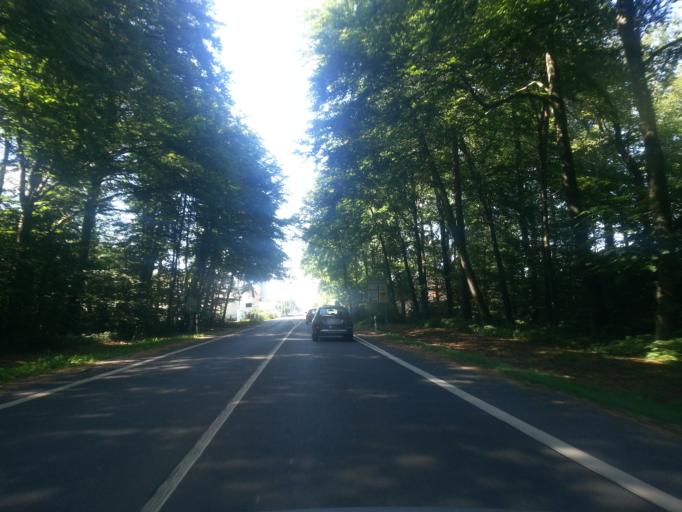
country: DE
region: Hesse
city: Heusenstamm
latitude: 50.0346
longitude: 8.7895
